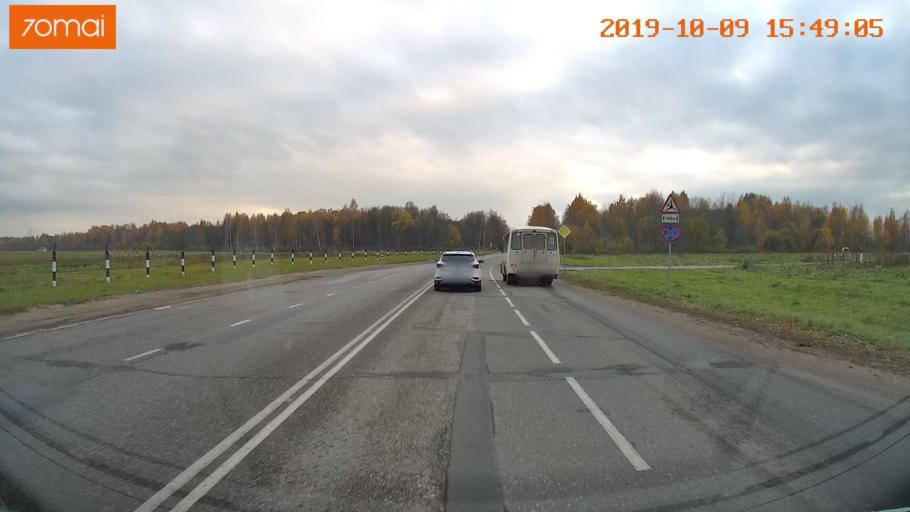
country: RU
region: Kostroma
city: Oktyabr'skiy
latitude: 57.8074
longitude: 41.0087
